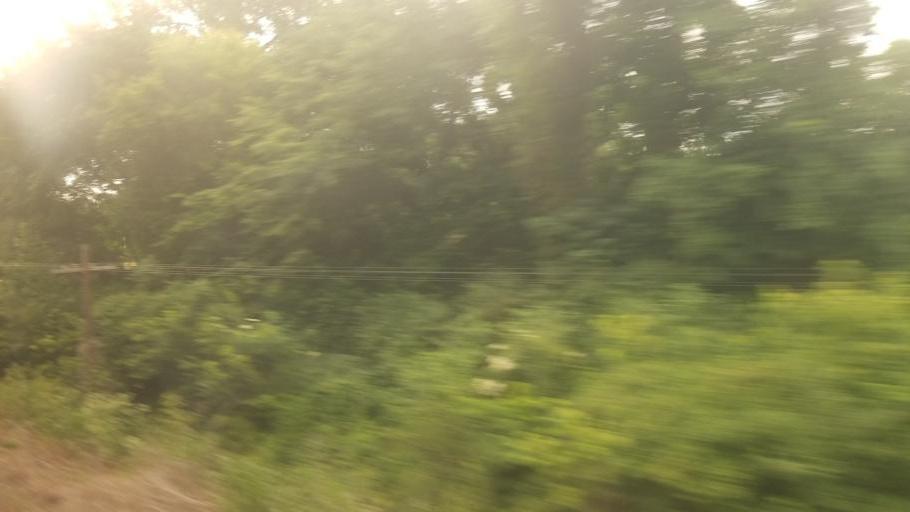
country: US
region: Kansas
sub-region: Shawnee County
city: Topeka
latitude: 39.0595
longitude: -95.5544
